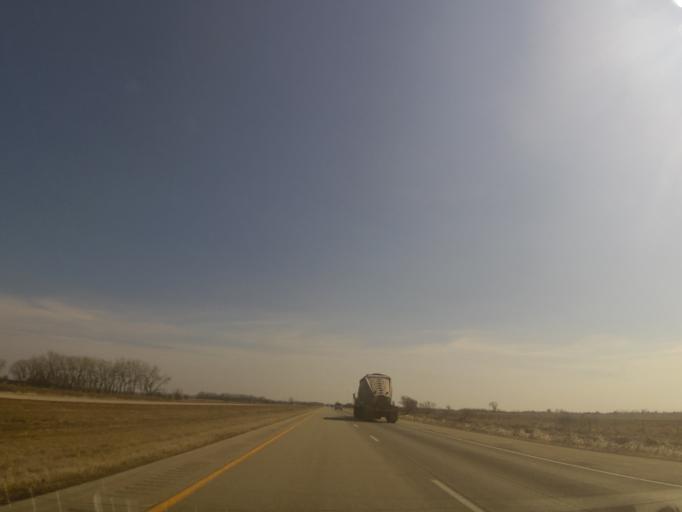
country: US
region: North Dakota
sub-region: Grand Forks County
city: Grand Forks
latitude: 48.0289
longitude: -97.1333
